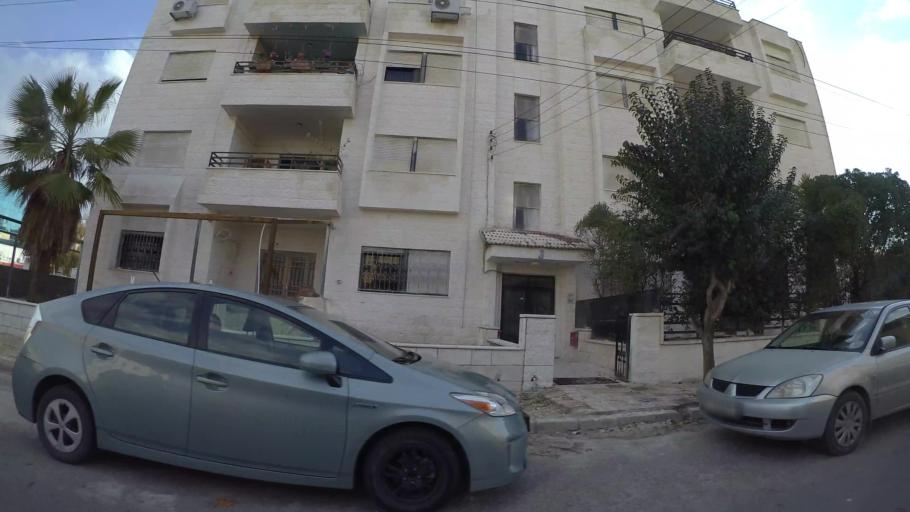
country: JO
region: Amman
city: Al Jubayhah
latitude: 31.9816
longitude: 35.8917
